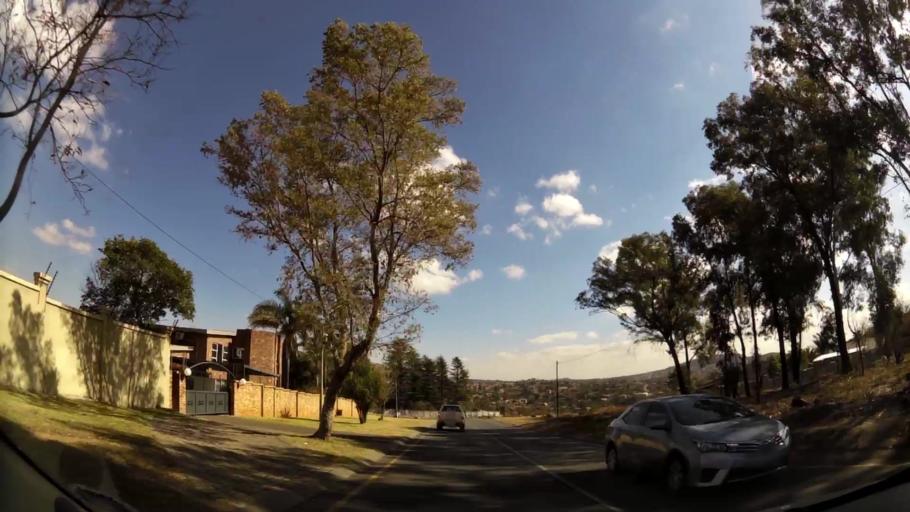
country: ZA
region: Gauteng
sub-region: City of Johannesburg Metropolitan Municipality
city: Roodepoort
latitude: -26.1039
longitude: 27.8429
